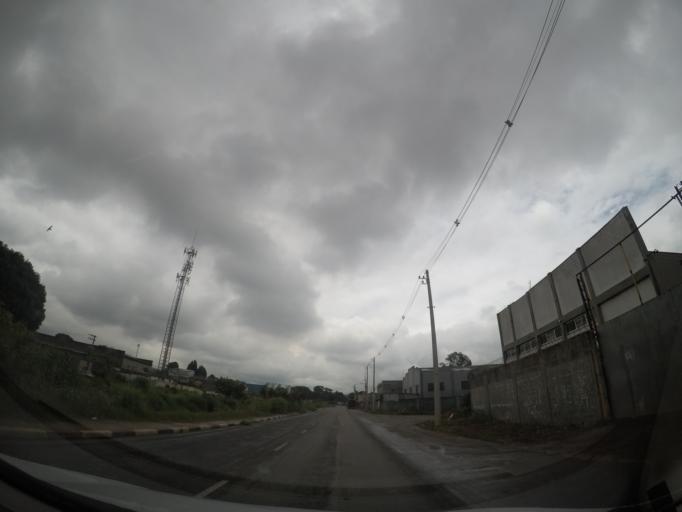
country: BR
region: Sao Paulo
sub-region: Guarulhos
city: Guarulhos
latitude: -23.4678
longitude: -46.4777
